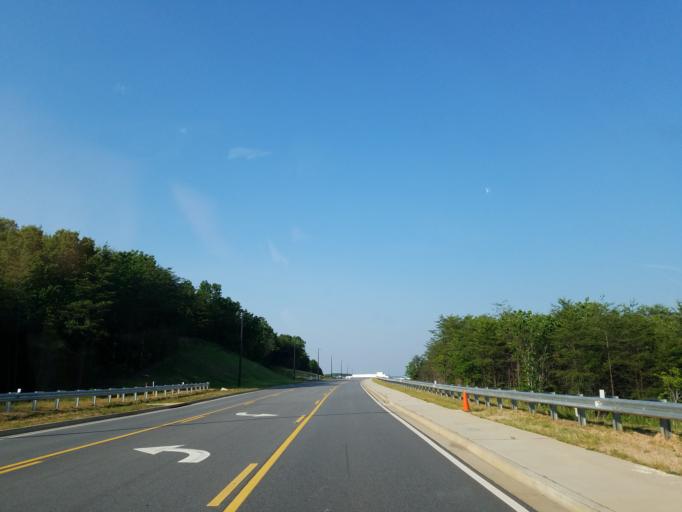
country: US
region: Georgia
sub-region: Forsyth County
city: Cumming
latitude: 34.2144
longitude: -84.1213
